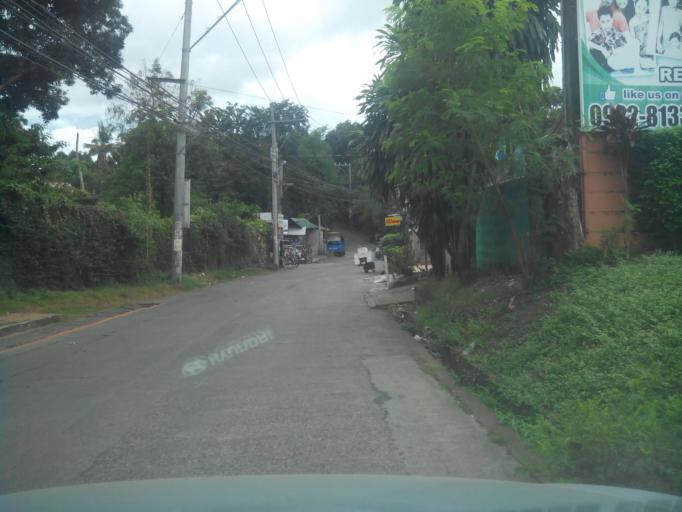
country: PH
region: Calabarzon
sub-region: Province of Rizal
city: Teresa
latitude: 14.6002
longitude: 121.1824
